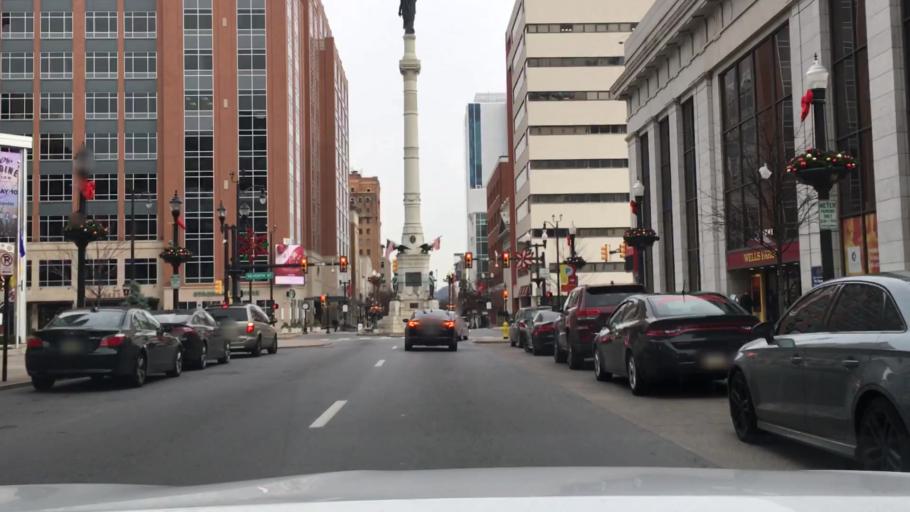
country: US
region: Pennsylvania
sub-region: Lehigh County
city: Allentown
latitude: 40.6020
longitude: -75.4724
